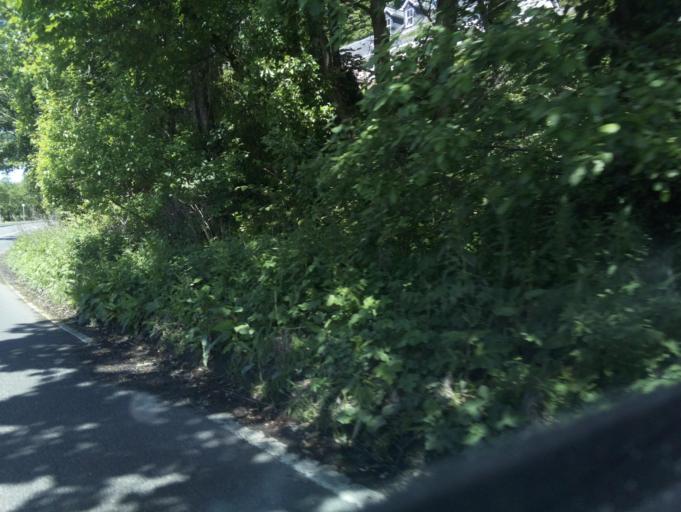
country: GB
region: Scotland
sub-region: Dumfries and Galloway
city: Langholm
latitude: 55.1458
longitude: -2.9922
